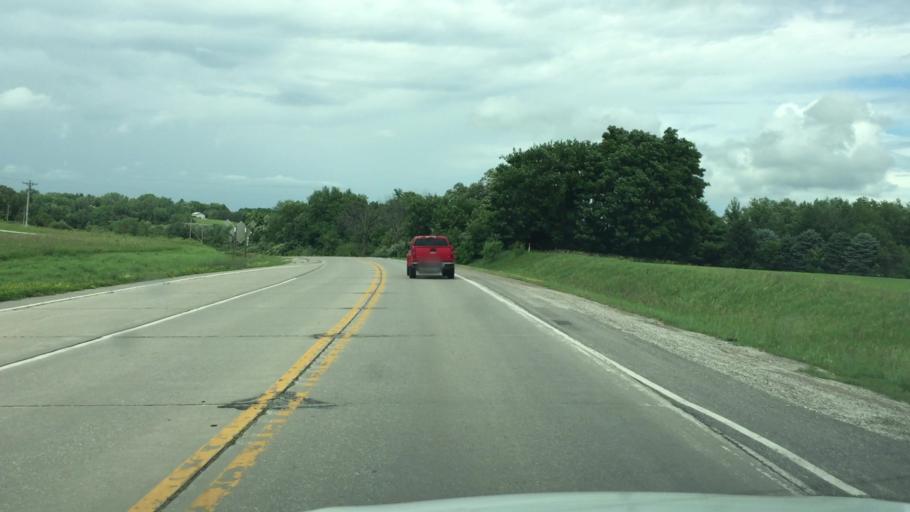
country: US
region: Iowa
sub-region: Jasper County
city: Newton
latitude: 41.7213
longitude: -93.0593
